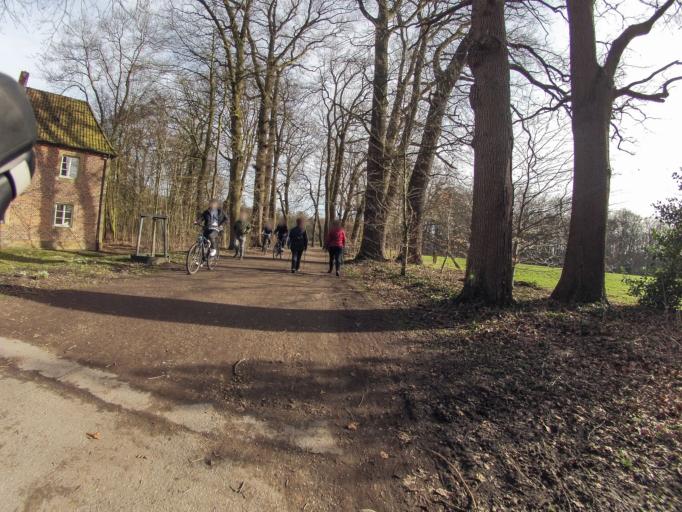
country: DE
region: North Rhine-Westphalia
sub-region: Regierungsbezirk Munster
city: Rheine
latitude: 52.3016
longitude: 7.4269
